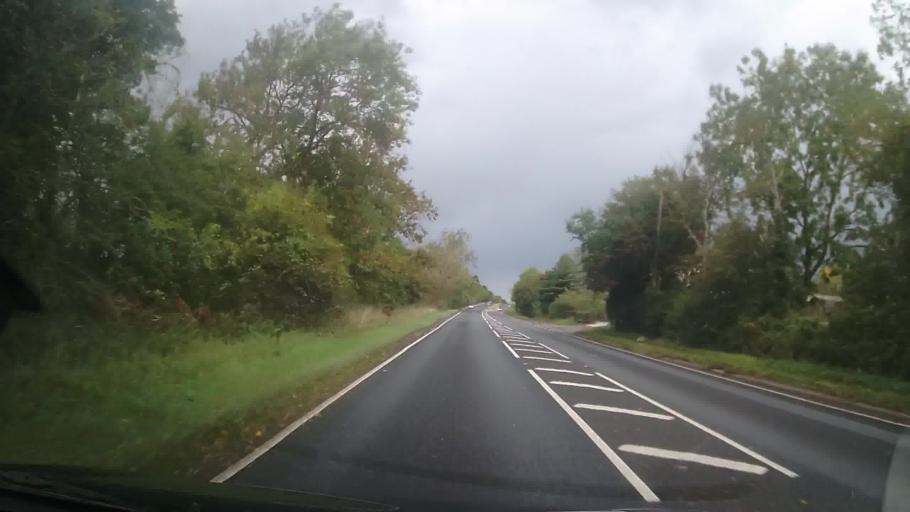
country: GB
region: England
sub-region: Worcestershire
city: Badsey
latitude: 52.0734
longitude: -1.9123
